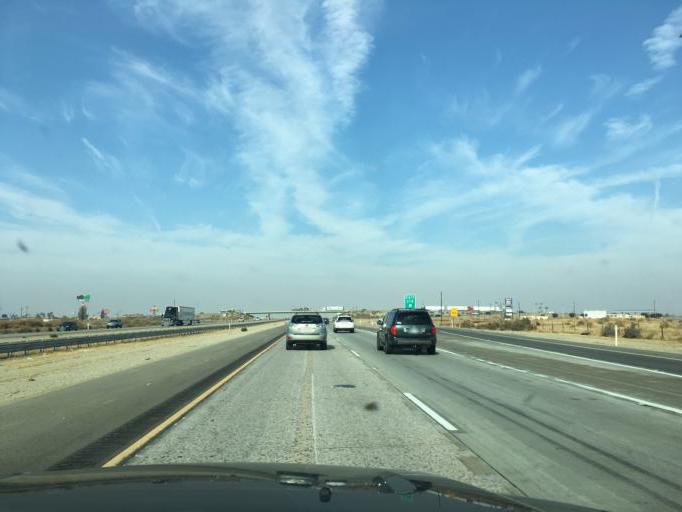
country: US
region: California
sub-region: Kern County
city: Lost Hills
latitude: 35.6119
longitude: -119.6499
